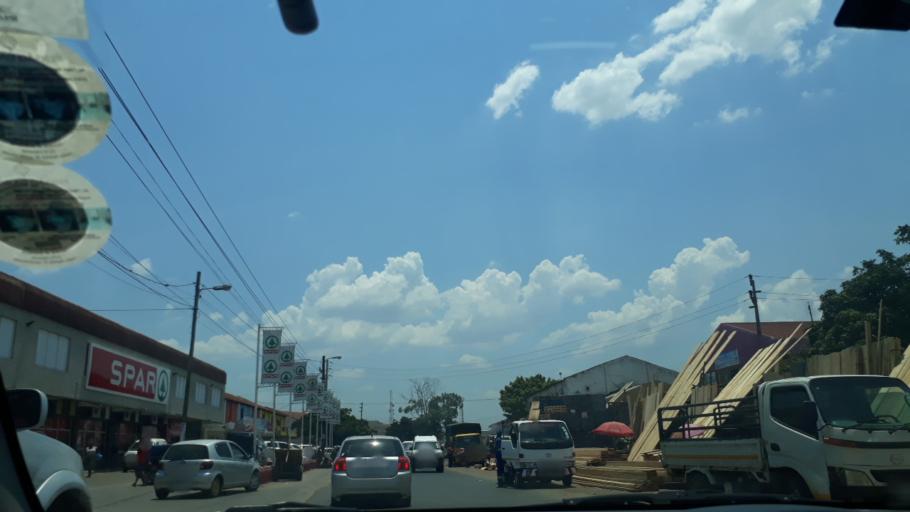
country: MZ
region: Maputo City
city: Maputo
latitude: -25.9355
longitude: 32.5551
